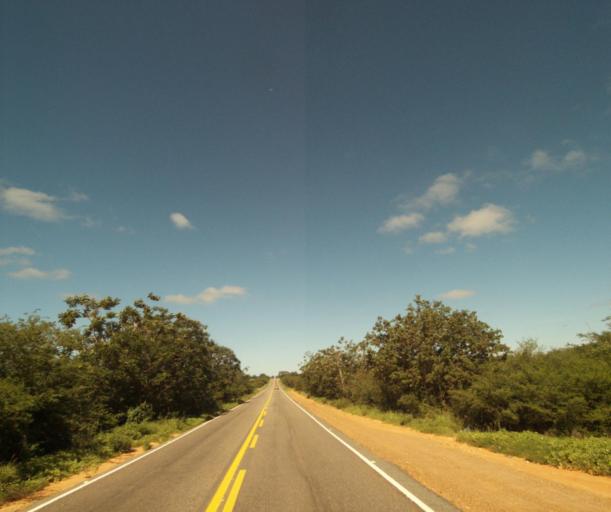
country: BR
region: Bahia
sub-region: Palmas De Monte Alto
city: Palmas de Monte Alto
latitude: -14.2434
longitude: -43.0860
